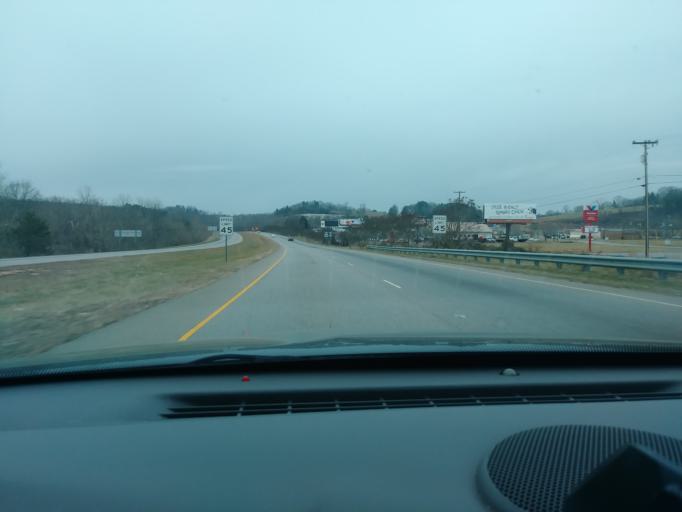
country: US
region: North Carolina
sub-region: Wilkes County
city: Wilkesboro
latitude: 36.1459
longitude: -81.1780
